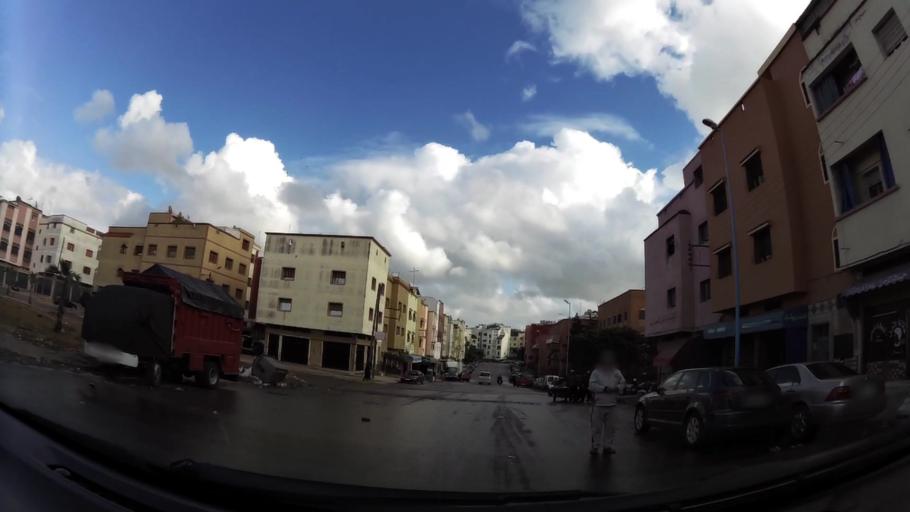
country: MA
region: Grand Casablanca
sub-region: Casablanca
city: Casablanca
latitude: 33.5438
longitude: -7.5911
